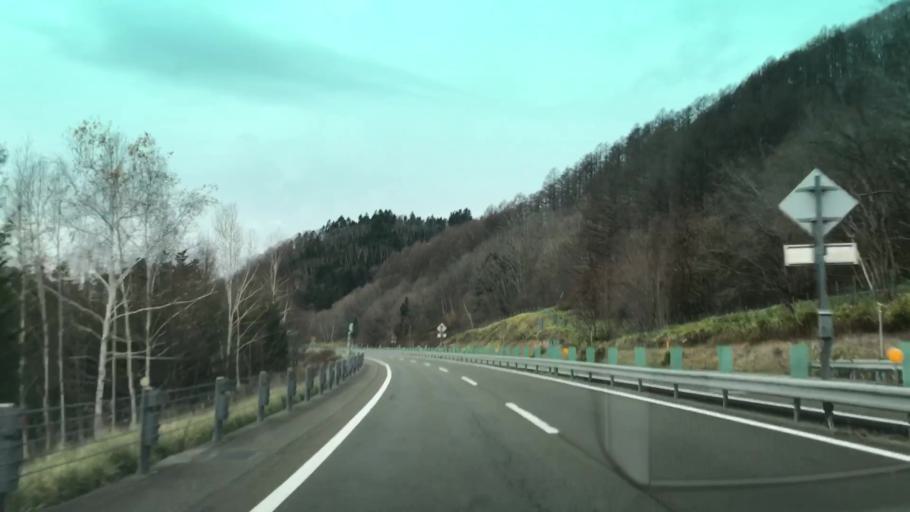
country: JP
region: Hokkaido
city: Chitose
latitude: 42.9071
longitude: 141.9982
